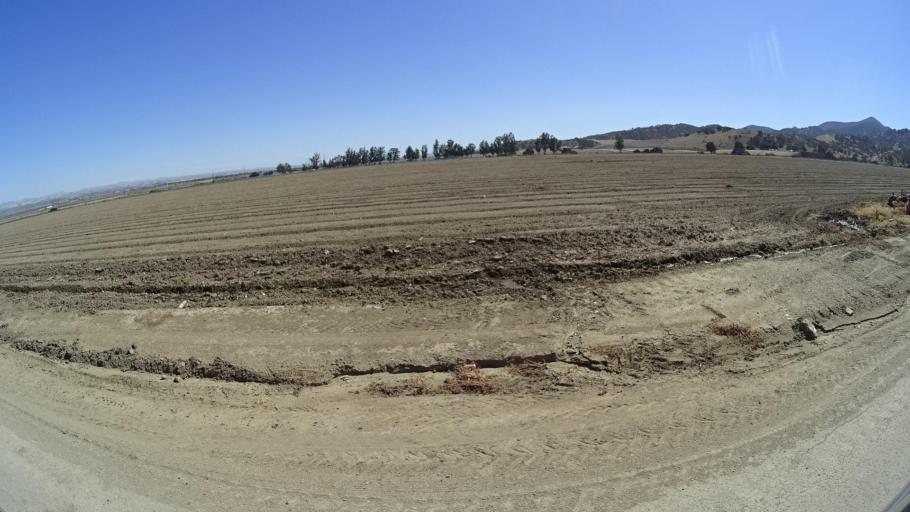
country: US
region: California
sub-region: Monterey County
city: King City
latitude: 36.2309
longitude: -121.1798
